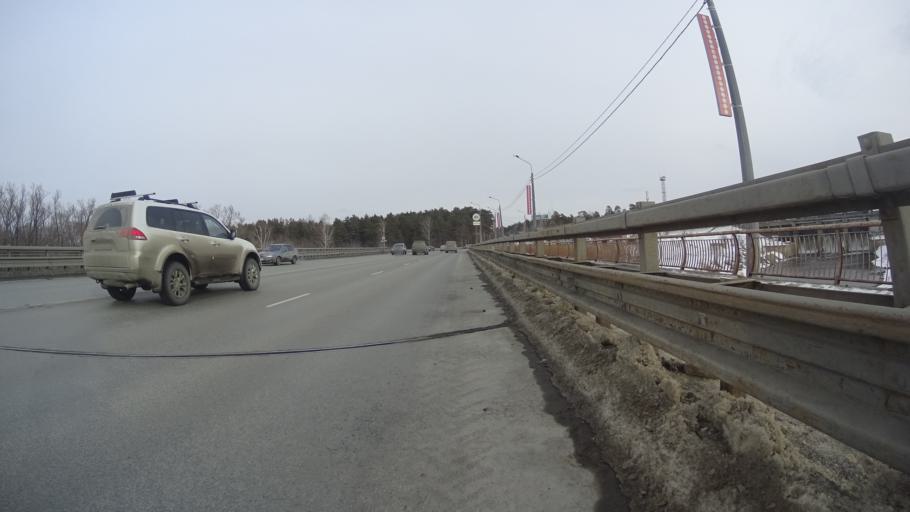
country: RU
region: Chelyabinsk
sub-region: Gorod Chelyabinsk
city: Chelyabinsk
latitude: 55.1482
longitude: 61.3247
